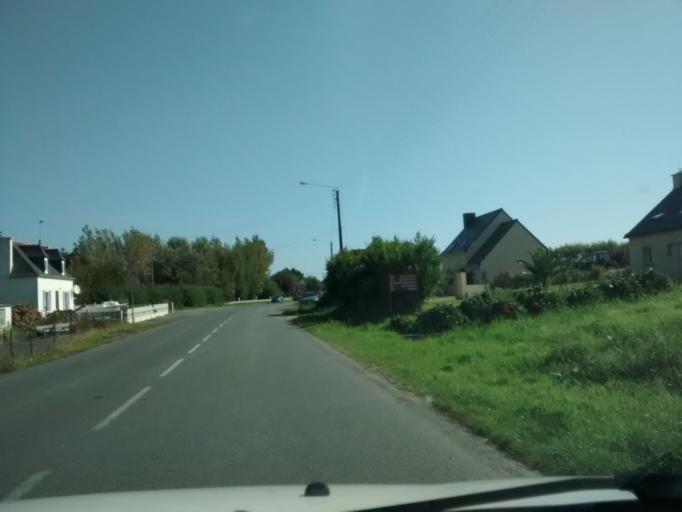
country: FR
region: Brittany
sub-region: Departement des Cotes-d'Armor
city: Pleubian
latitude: 48.8570
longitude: -3.1116
